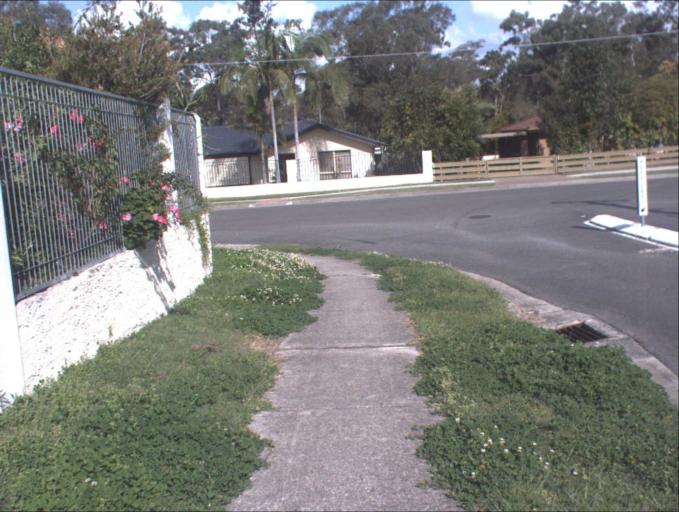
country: AU
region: Queensland
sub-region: Brisbane
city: Sunnybank Hills
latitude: -27.6687
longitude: 153.0466
